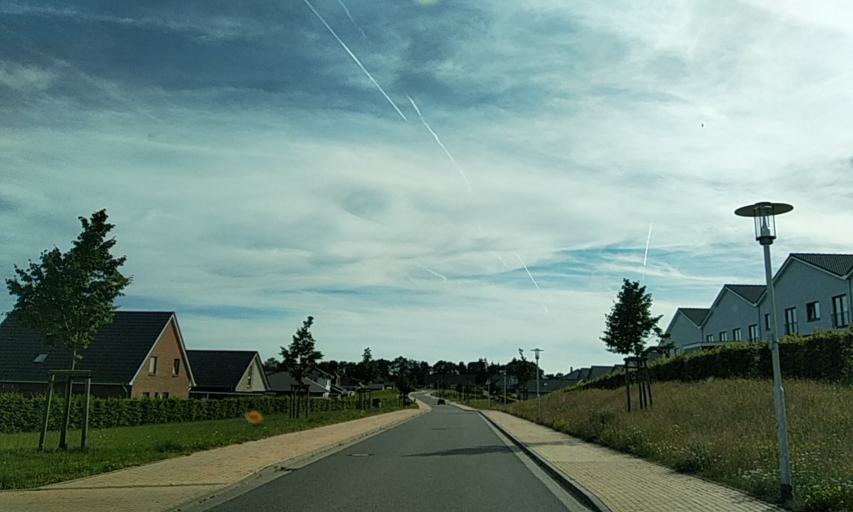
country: DE
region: Schleswig-Holstein
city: Schleswig
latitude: 54.5372
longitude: 9.5664
